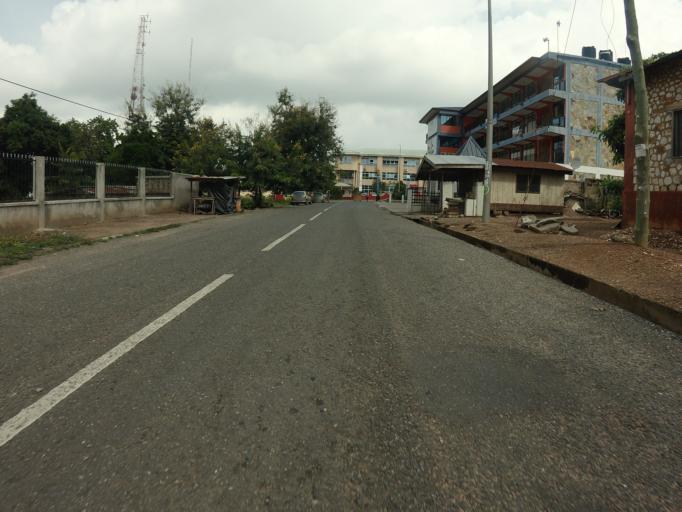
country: GH
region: Volta
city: Ho
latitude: 6.6117
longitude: 0.4691
